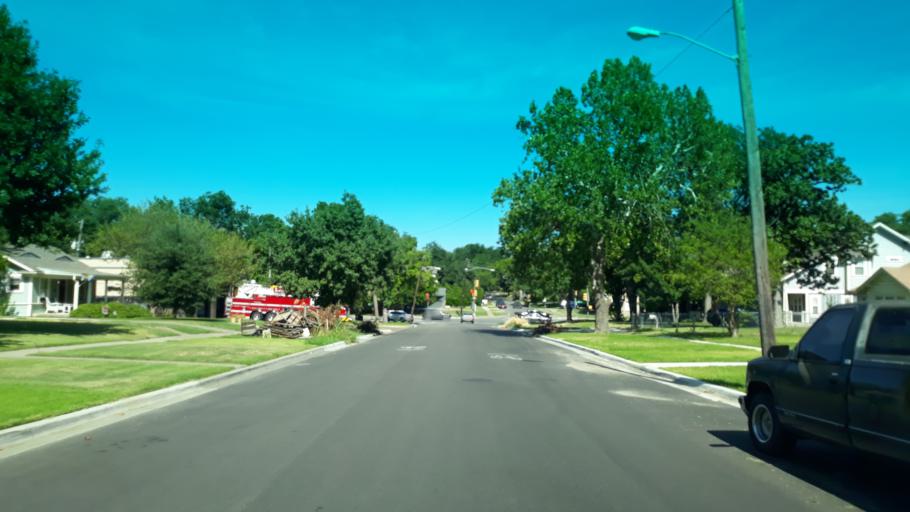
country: US
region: Texas
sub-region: Dallas County
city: Highland Park
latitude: 32.8174
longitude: -96.7628
